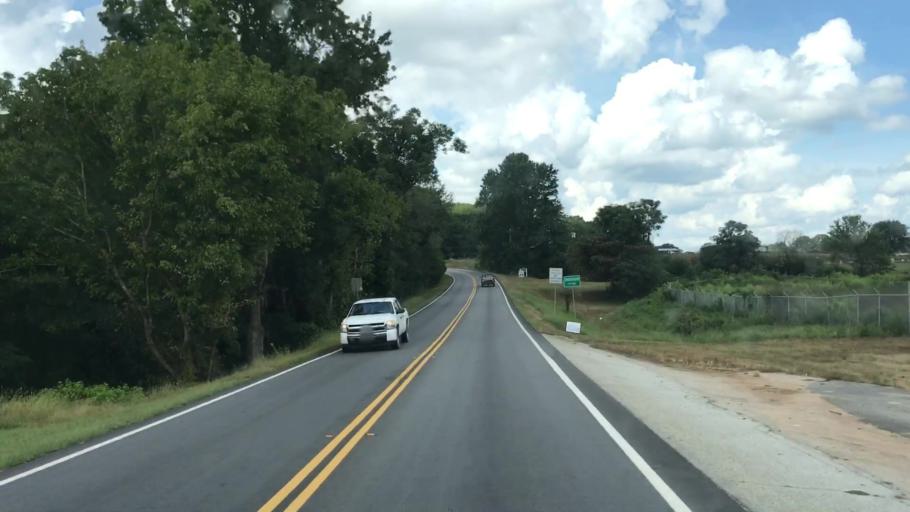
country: US
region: Georgia
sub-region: Greene County
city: Greensboro
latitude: 33.5709
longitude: -83.1664
